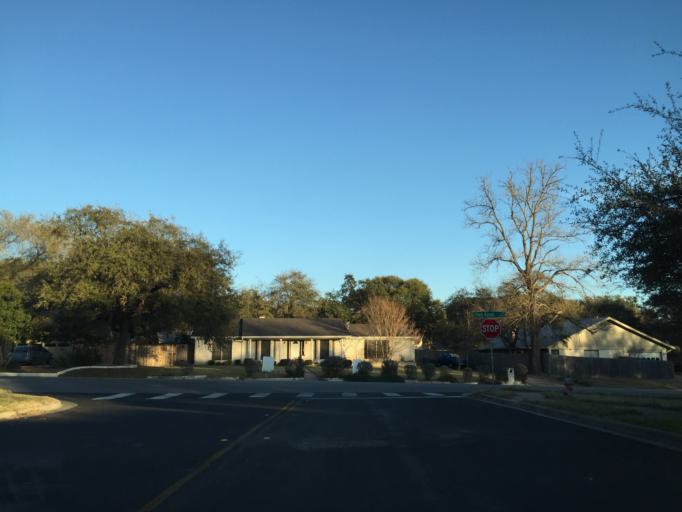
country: US
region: Texas
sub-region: Williamson County
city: Jollyville
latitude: 30.4232
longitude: -97.7631
